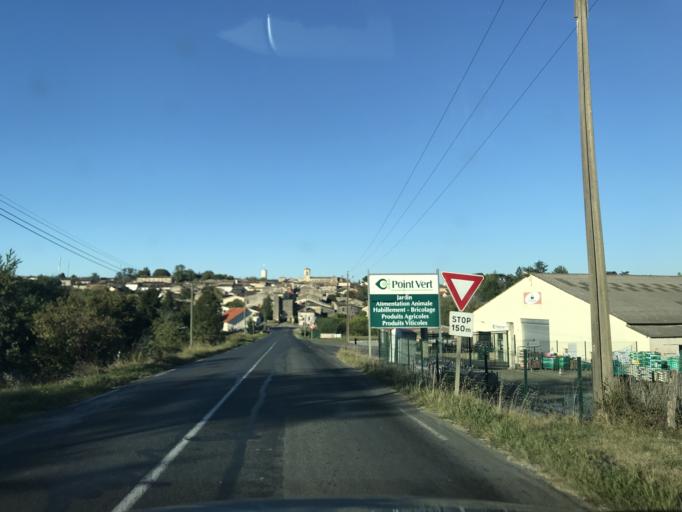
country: FR
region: Aquitaine
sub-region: Departement de la Gironde
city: Sauveterre-de-Guyenne
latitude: 44.6891
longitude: -0.0899
